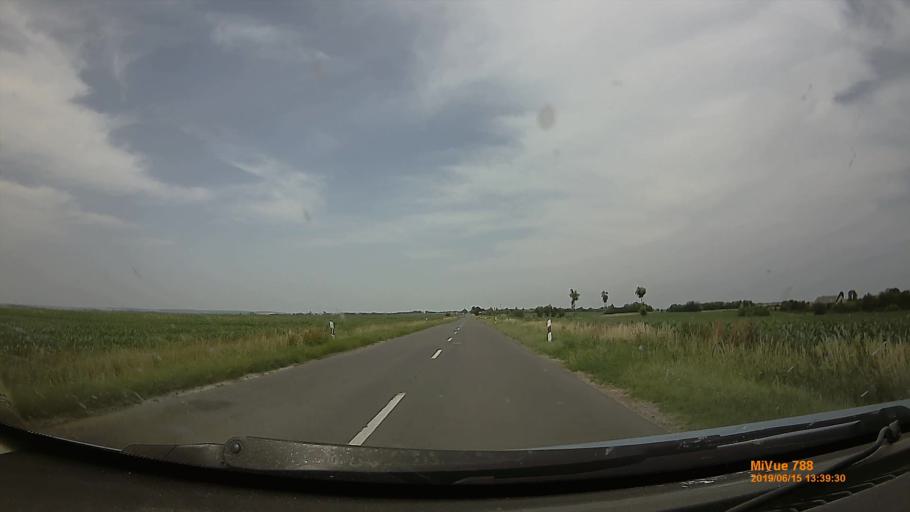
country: HU
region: Tolna
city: Iregszemcse
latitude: 46.6301
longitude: 18.2005
